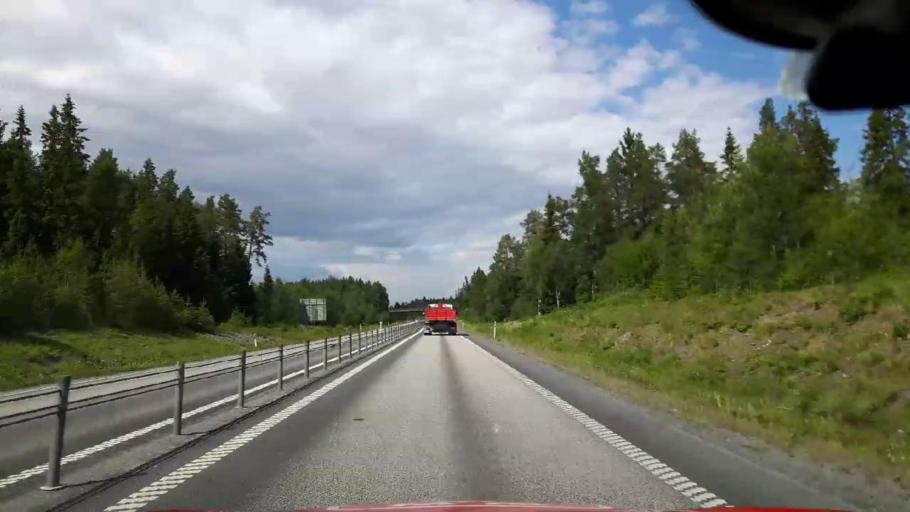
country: SE
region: Jaemtland
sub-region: OEstersunds Kommun
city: Ostersund
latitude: 63.2089
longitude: 14.6663
